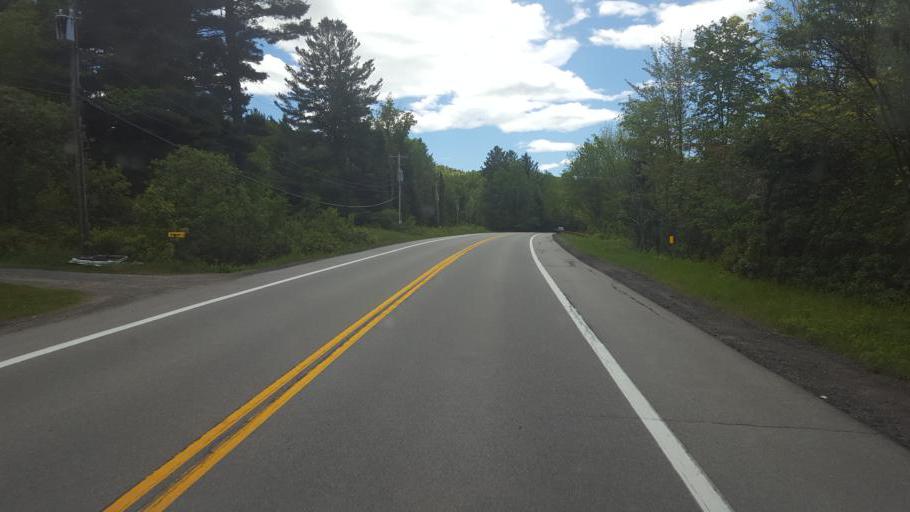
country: US
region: New York
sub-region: Hamilton County
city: Lake Pleasant
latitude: 43.4639
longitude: -74.4320
